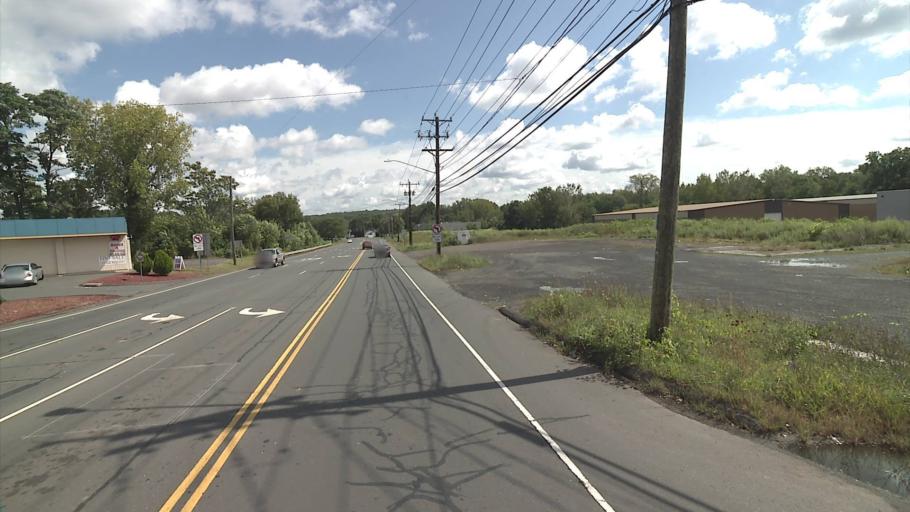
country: US
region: Connecticut
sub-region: Hartford County
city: Kensington
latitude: 41.6413
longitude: -72.7331
